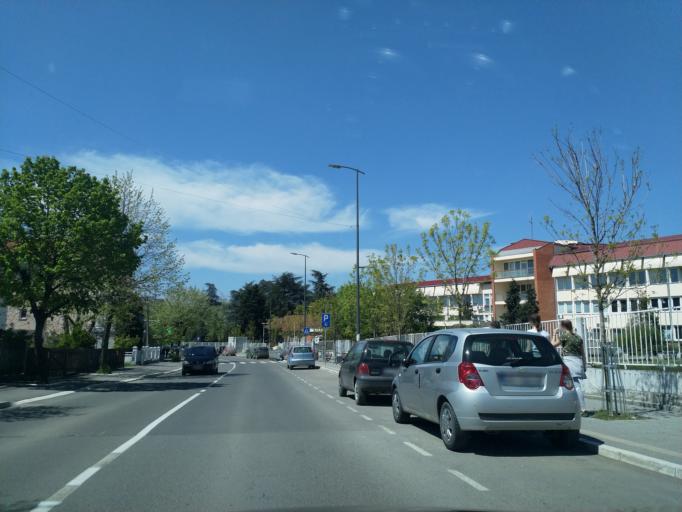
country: RS
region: Central Serbia
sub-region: Belgrade
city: Lazarevac
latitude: 44.3811
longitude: 20.2764
